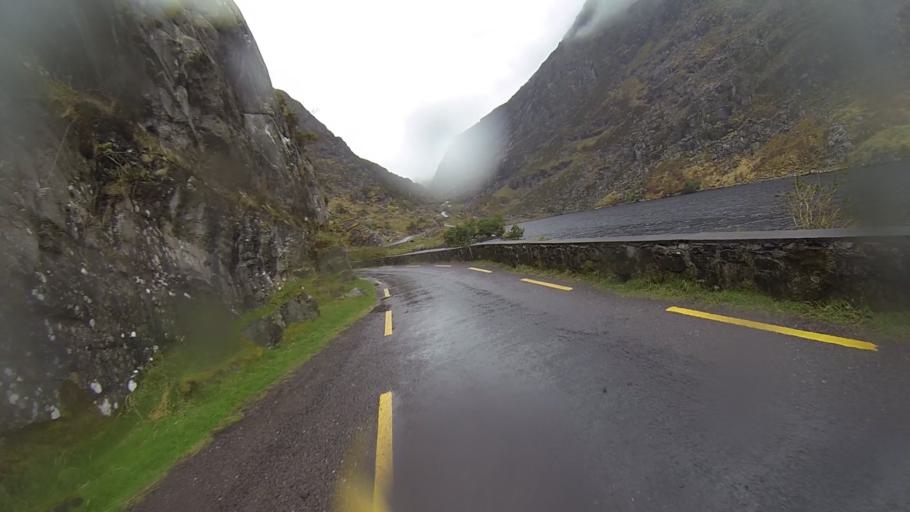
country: IE
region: Munster
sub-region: Ciarrai
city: Cill Airne
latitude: 52.0125
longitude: -9.6368
